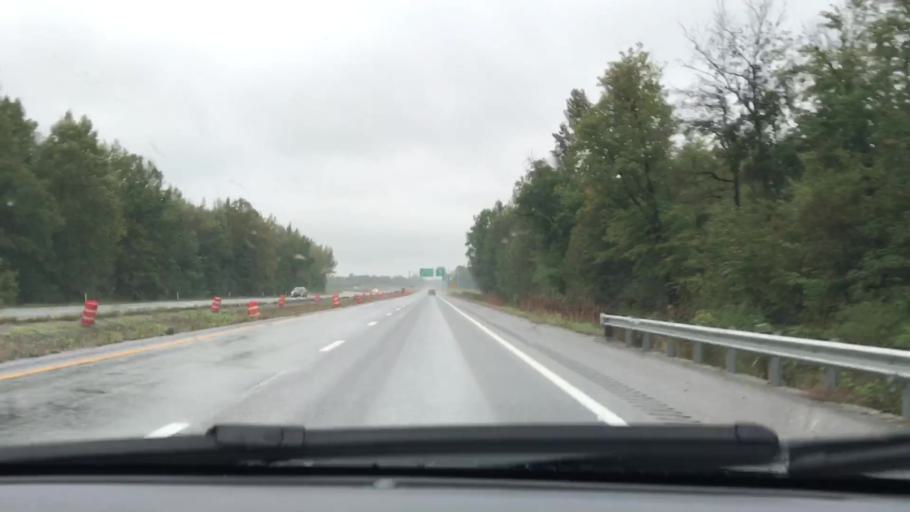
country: US
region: Kentucky
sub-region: Hopkins County
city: Nortonville
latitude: 37.1576
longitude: -87.4602
